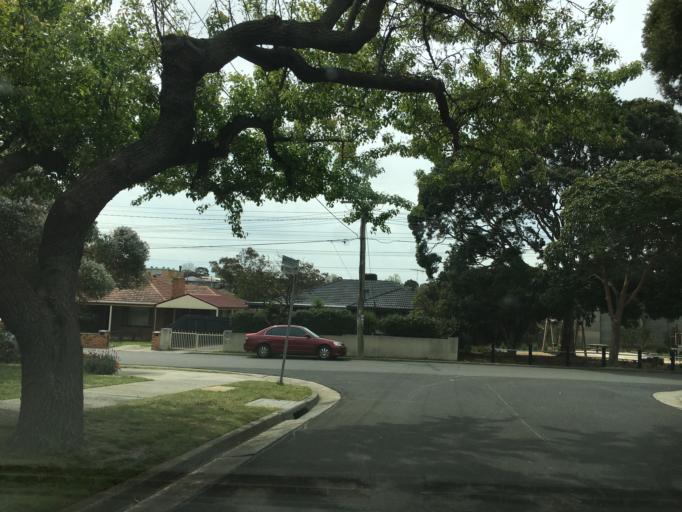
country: AU
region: Victoria
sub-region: Monash
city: Chadstone
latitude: -37.8868
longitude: 145.1028
